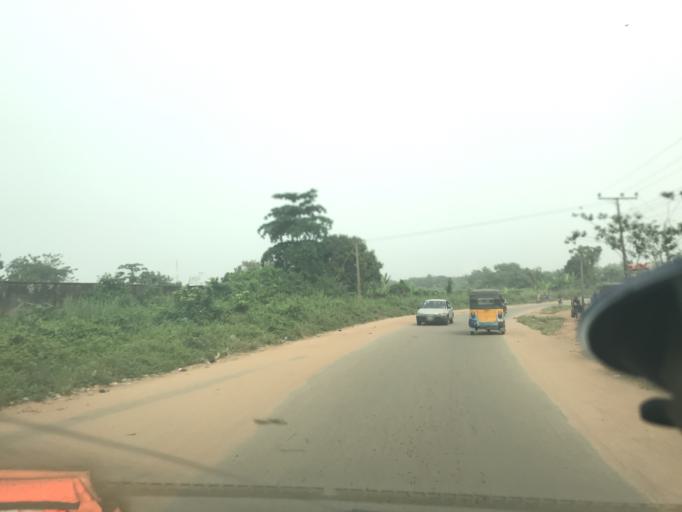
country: NG
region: Ogun
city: Ado Odo
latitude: 6.5030
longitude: 2.9529
